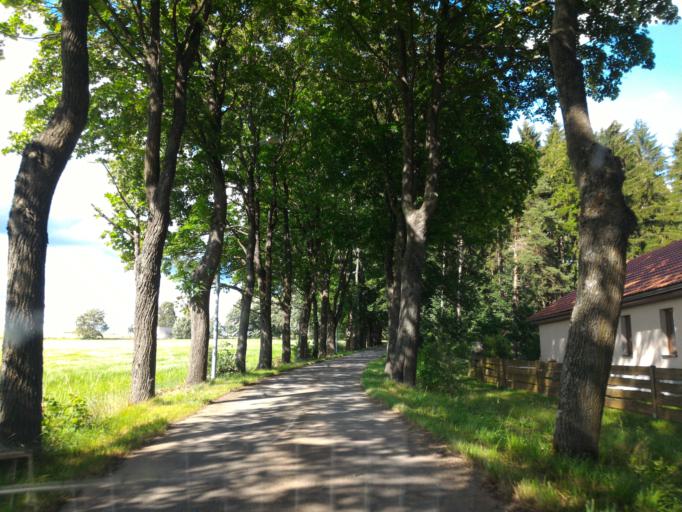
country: CZ
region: Vysocina
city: Velky Beranov
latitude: 49.4118
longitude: 15.6311
